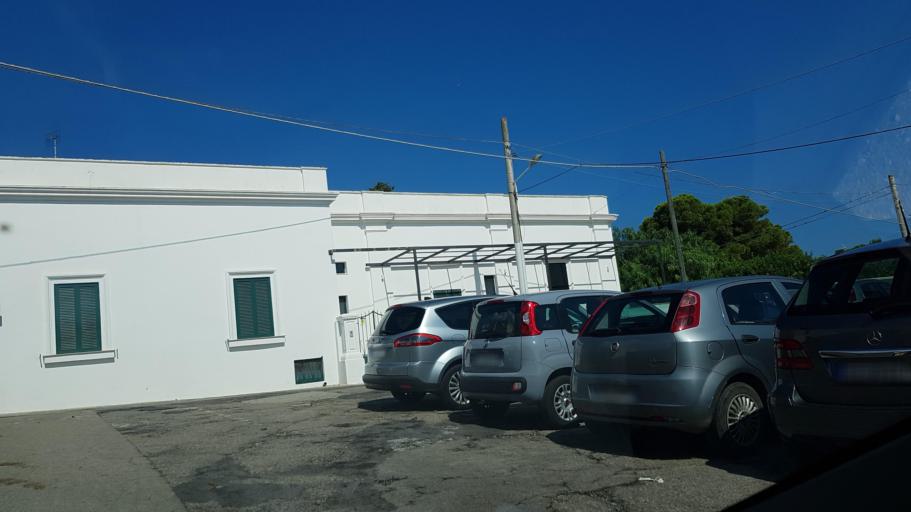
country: IT
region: Apulia
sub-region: Provincia di Lecce
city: Leuca
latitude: 39.7983
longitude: 18.3569
